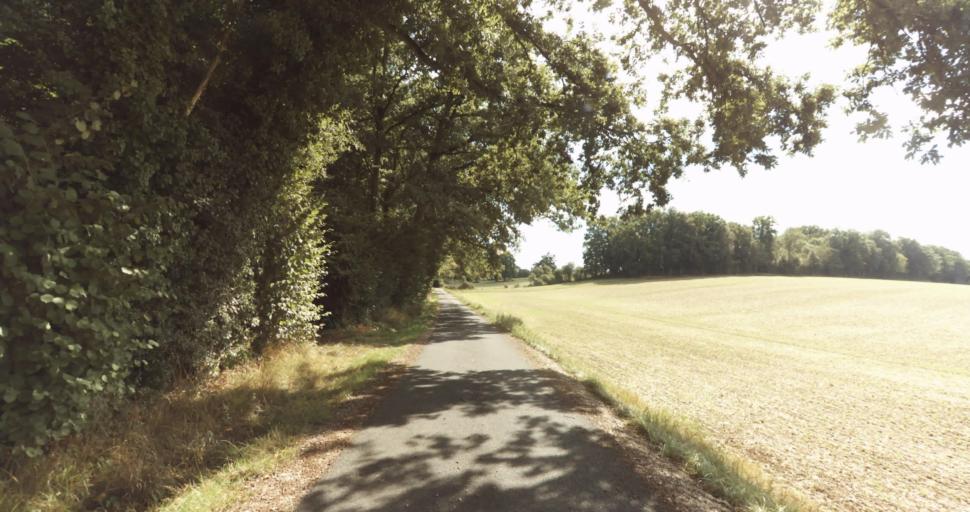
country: FR
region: Lower Normandy
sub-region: Departement du Calvados
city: Orbec
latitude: 48.9116
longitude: 0.3839
